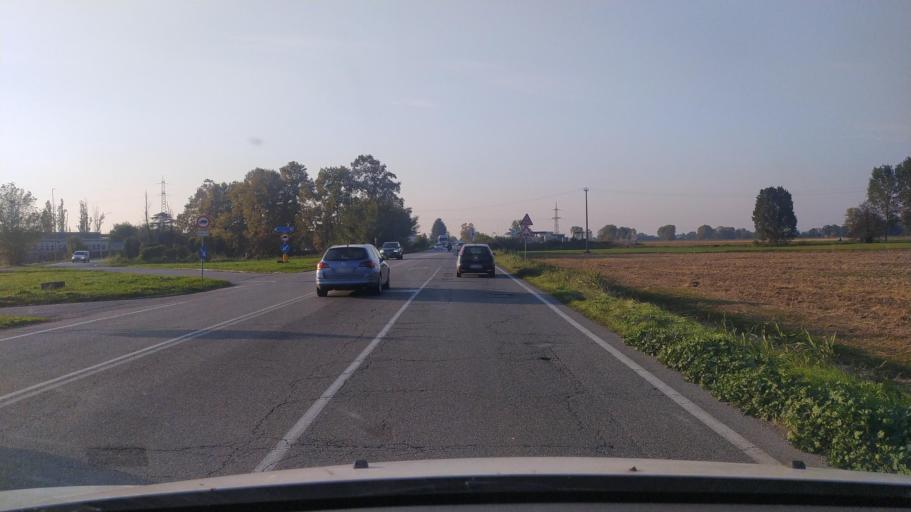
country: IT
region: Lombardy
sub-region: Provincia di Lodi
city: Zelo Buon Persico
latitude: 45.4073
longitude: 9.4459
